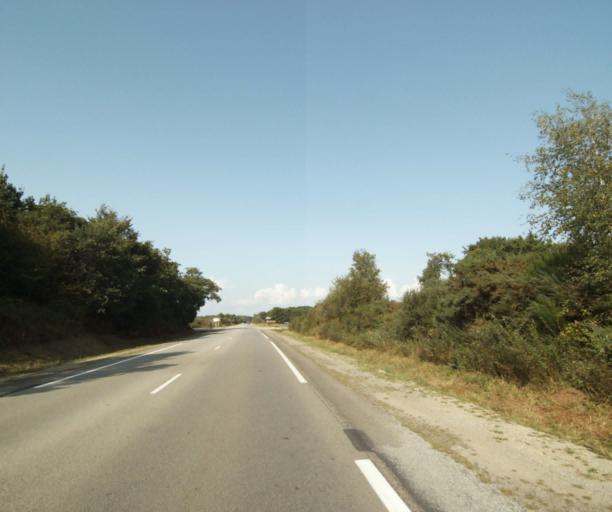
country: FR
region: Brittany
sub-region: Departement du Morbihan
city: Riantec
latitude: 47.7391
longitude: -3.3034
